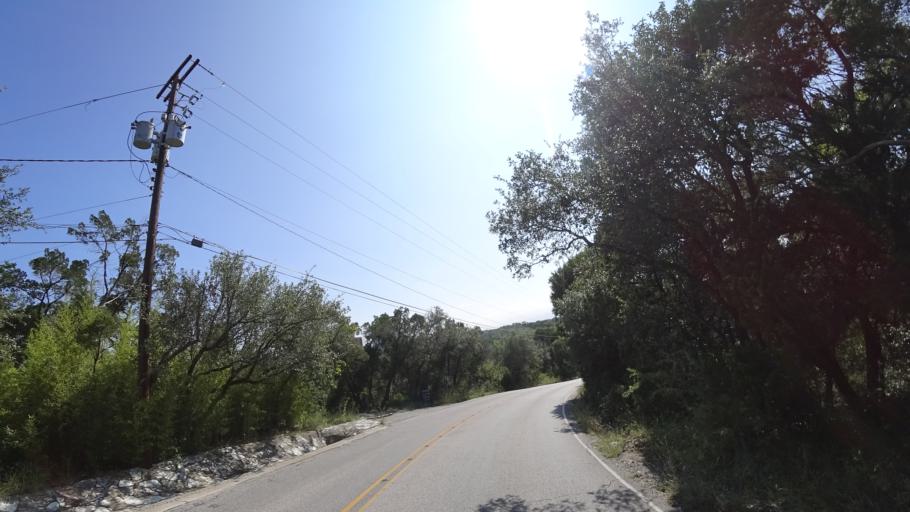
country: US
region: Texas
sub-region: Travis County
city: West Lake Hills
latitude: 30.2934
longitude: -97.7979
